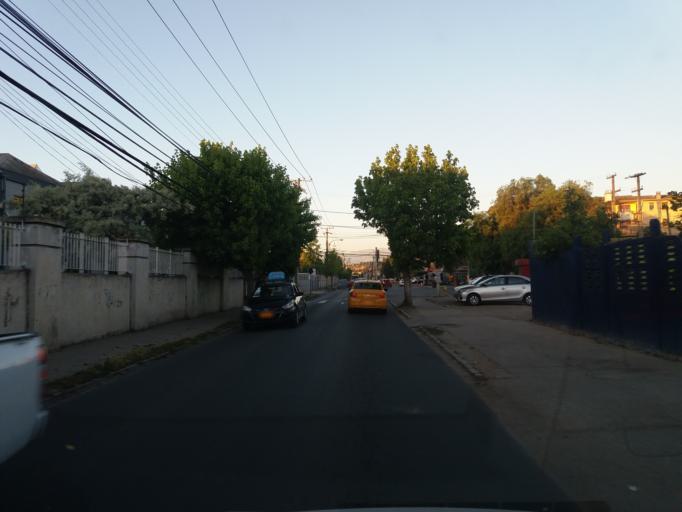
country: CL
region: Valparaiso
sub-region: Provincia de Quillota
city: Quillota
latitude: -32.8921
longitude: -71.2627
